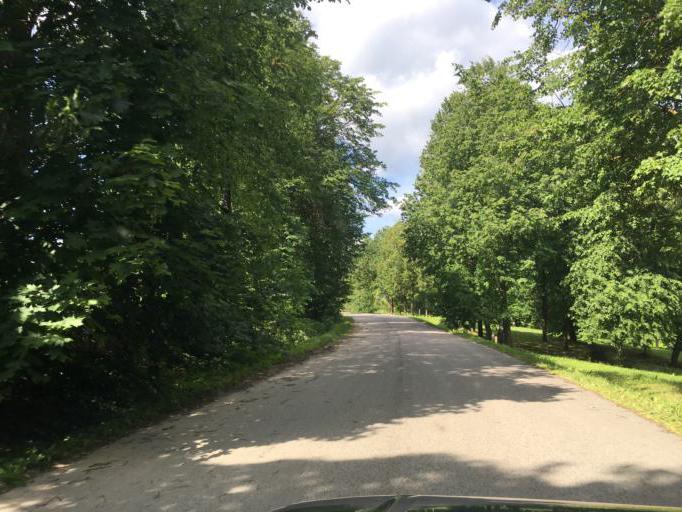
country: LV
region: Balvu Rajons
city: Balvi
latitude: 57.1343
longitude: 27.2658
